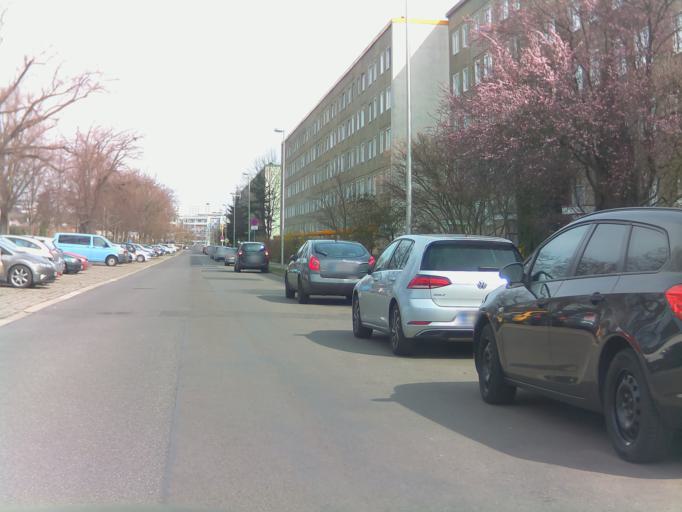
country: DE
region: Brandenburg
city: Cottbus
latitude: 51.7598
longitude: 14.3083
